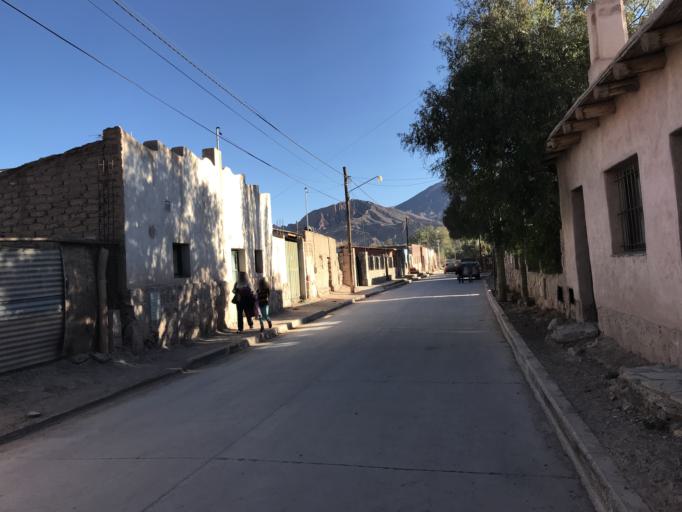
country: AR
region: Jujuy
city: Maimara
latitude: -23.5773
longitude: -65.4002
